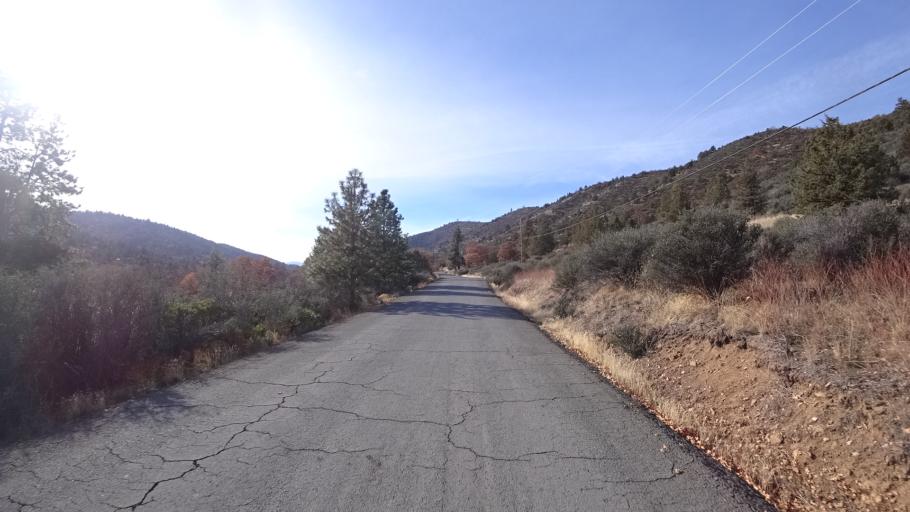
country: US
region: California
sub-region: Siskiyou County
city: Montague
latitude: 41.6211
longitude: -122.5765
